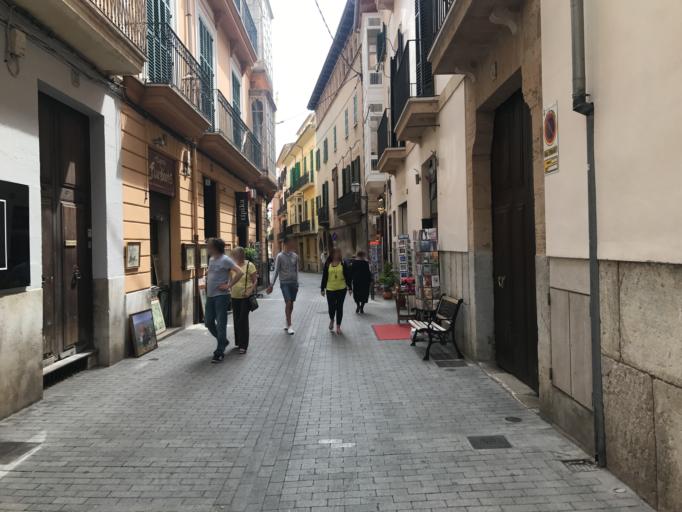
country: ES
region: Balearic Islands
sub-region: Illes Balears
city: Palma
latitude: 39.5684
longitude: 2.6509
